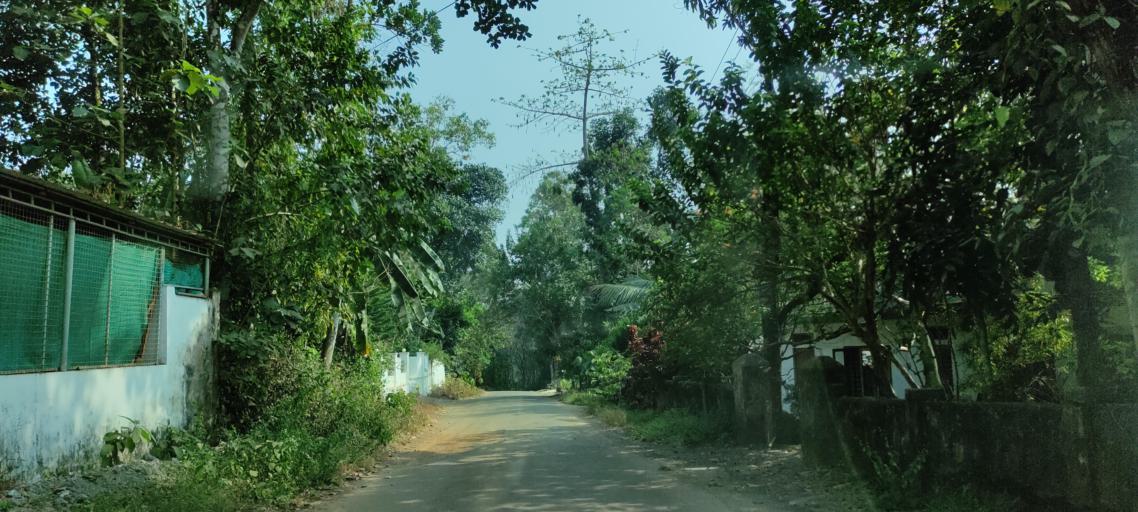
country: IN
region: Kerala
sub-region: Ernakulam
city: Piravam
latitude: 9.8215
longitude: 76.5131
